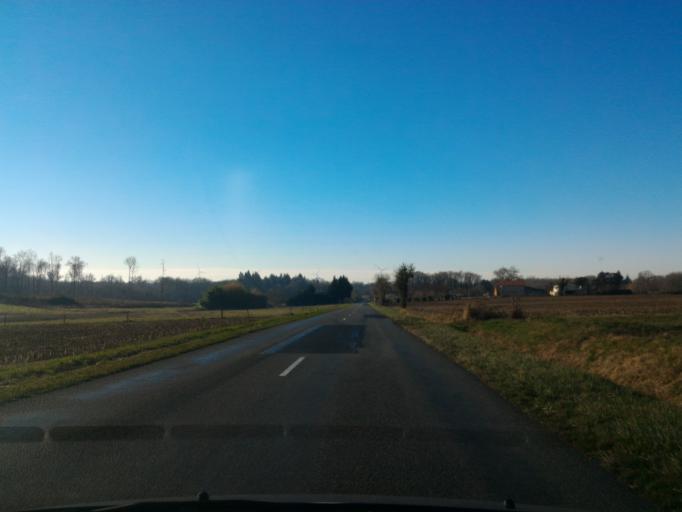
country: FR
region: Poitou-Charentes
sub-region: Departement de la Charente
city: Champagne-Mouton
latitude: 46.0070
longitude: 0.4832
